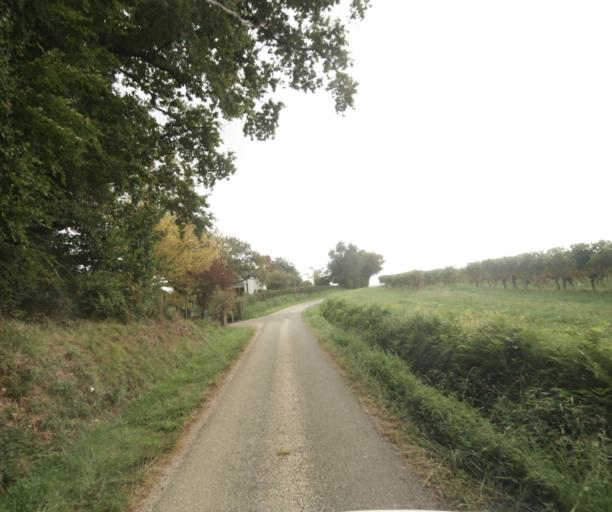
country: FR
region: Midi-Pyrenees
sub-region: Departement du Gers
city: Nogaro
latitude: 43.8319
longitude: -0.0679
